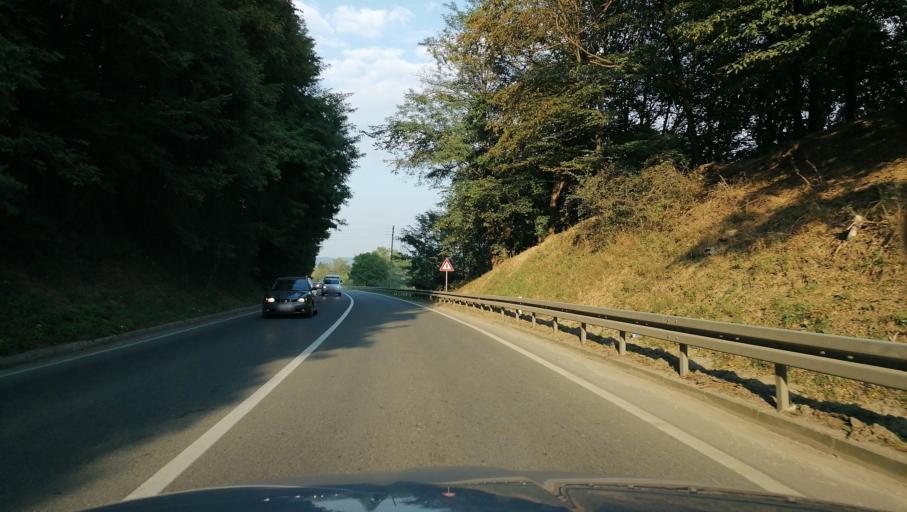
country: RS
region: Central Serbia
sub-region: Zlatiborski Okrug
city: Pozega
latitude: 43.8091
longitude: 20.0267
